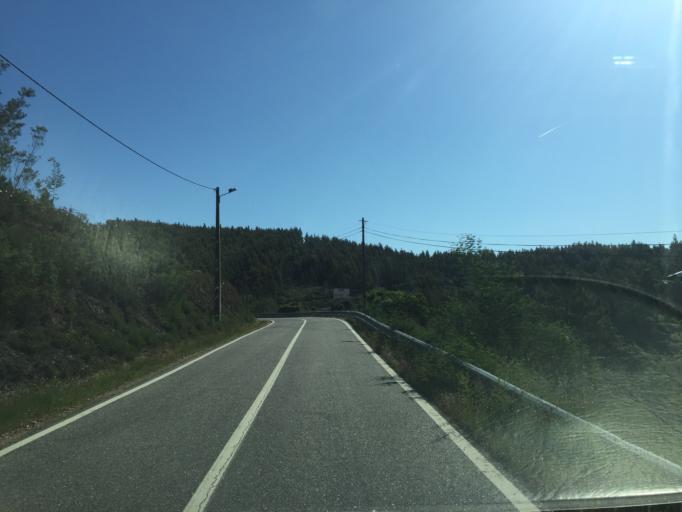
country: PT
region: Coimbra
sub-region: Pampilhosa da Serra
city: Pampilhosa da Serra
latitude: 40.0483
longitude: -7.8729
